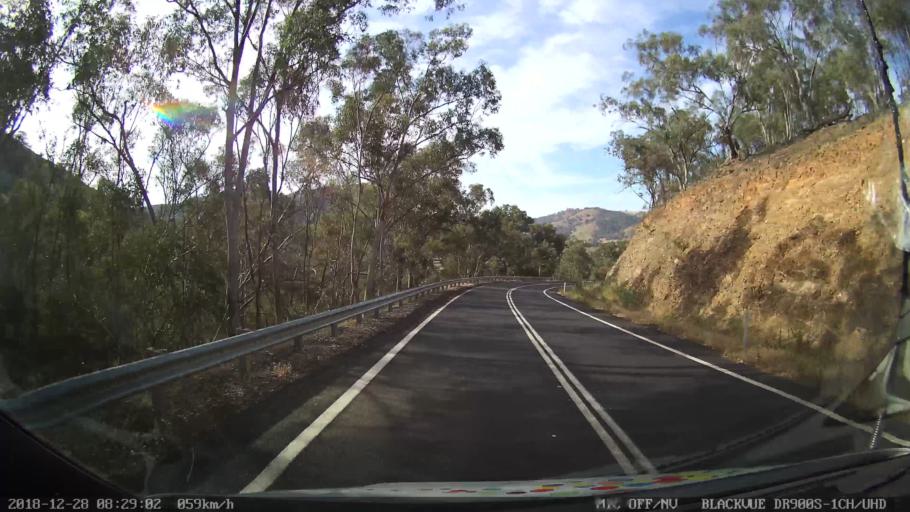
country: AU
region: New South Wales
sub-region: Blayney
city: Blayney
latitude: -33.9456
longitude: 149.3237
